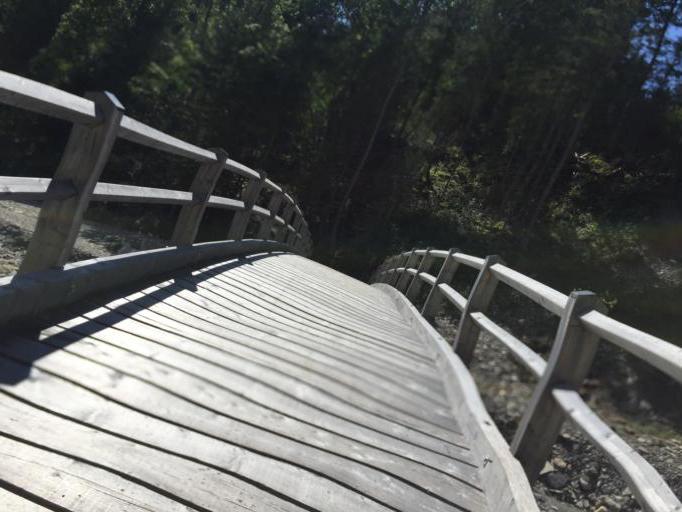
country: CH
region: Bern
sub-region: Frutigen-Niedersimmental District
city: Adelboden
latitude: 46.4854
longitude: 7.5297
